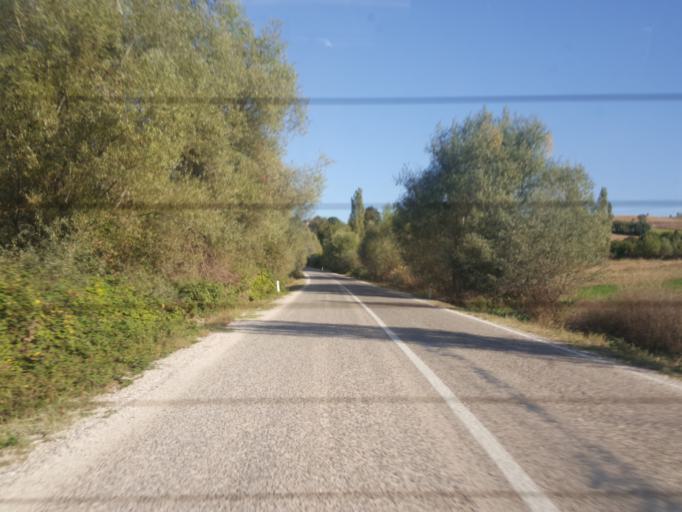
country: TR
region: Amasya
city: Tasova
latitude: 40.7153
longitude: 36.3185
